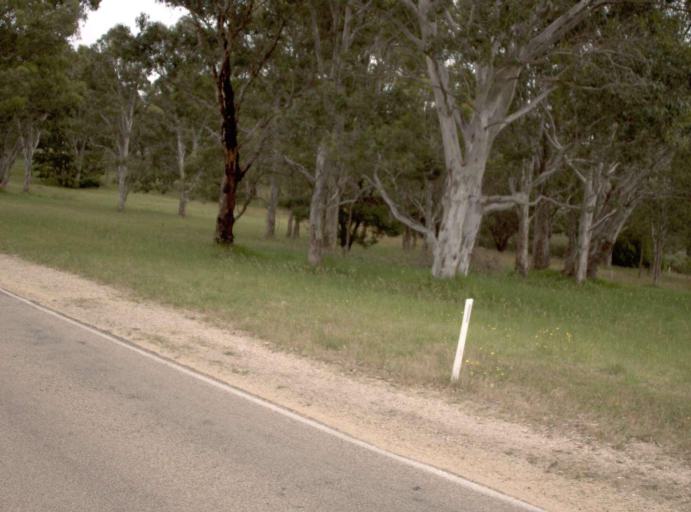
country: AU
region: Victoria
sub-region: East Gippsland
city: Bairnsdale
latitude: -37.7952
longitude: 147.6098
